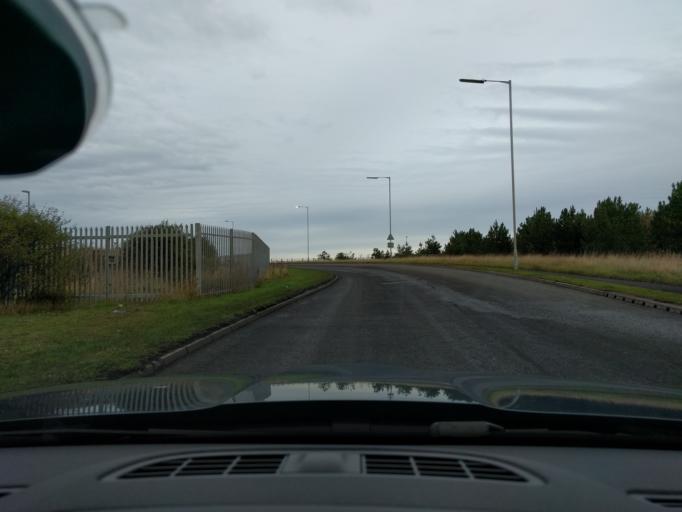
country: GB
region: England
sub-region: Northumberland
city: Blyth
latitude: 55.1363
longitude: -1.5121
